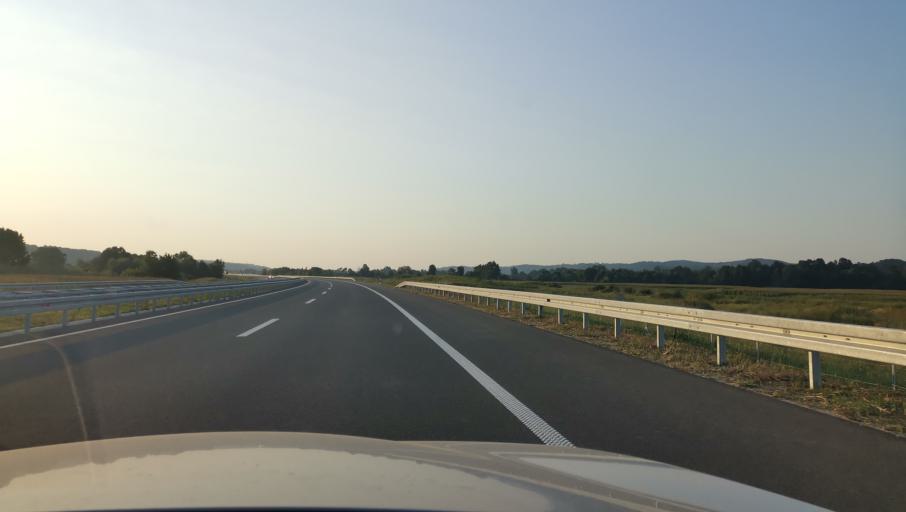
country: RS
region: Central Serbia
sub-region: Kolubarski Okrug
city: Ljig
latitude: 44.3042
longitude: 20.2306
